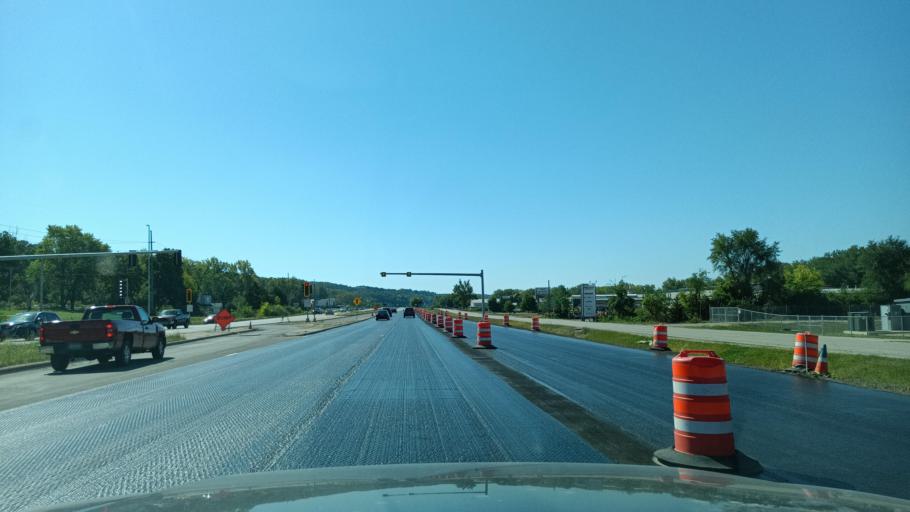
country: US
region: Illinois
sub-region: Peoria County
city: North Peoria
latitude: 40.7073
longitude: -89.5343
